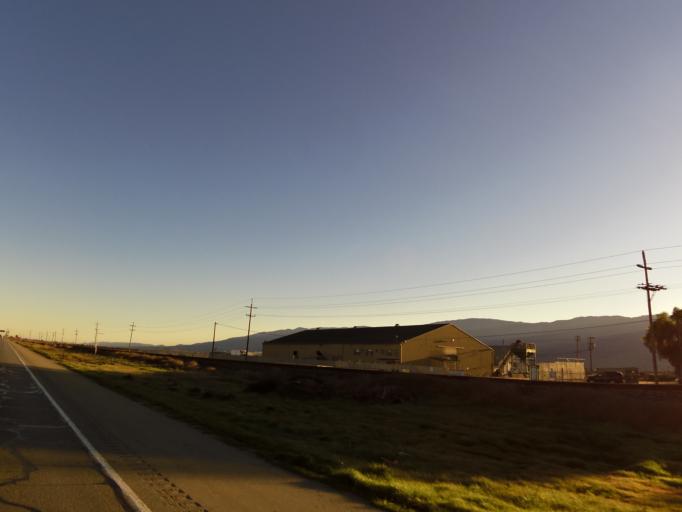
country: US
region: California
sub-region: Monterey County
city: Gonzales
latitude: 36.5293
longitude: -121.4729
